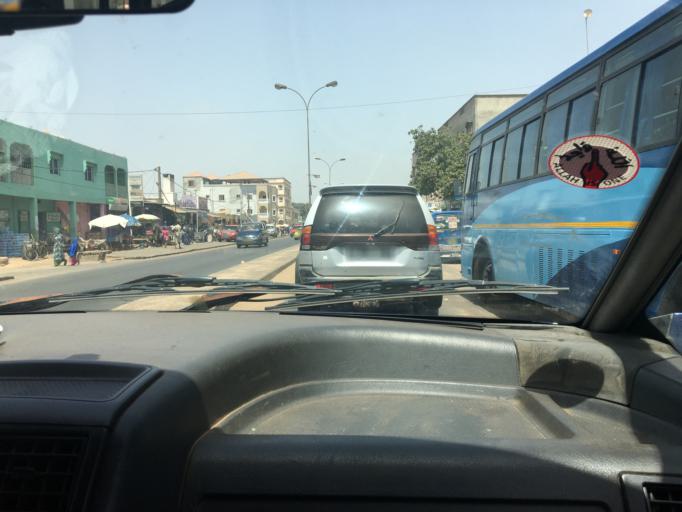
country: GM
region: Western
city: Abuko
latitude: 13.4069
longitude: -16.6660
